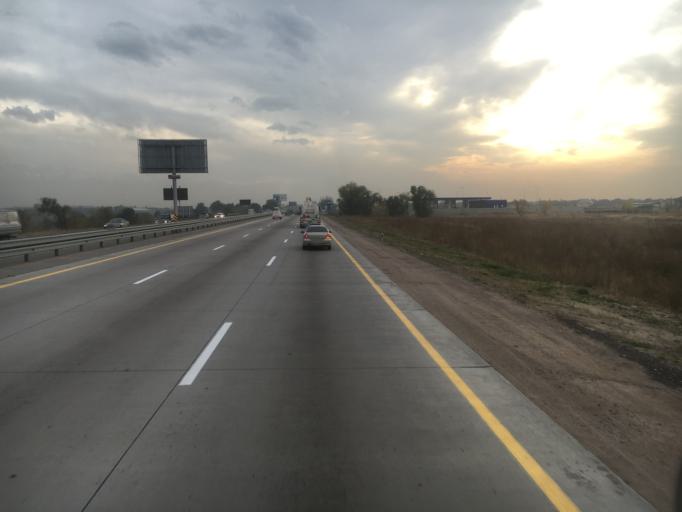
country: KZ
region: Almaty Oblysy
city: Pervomayskiy
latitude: 43.3844
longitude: 76.9647
